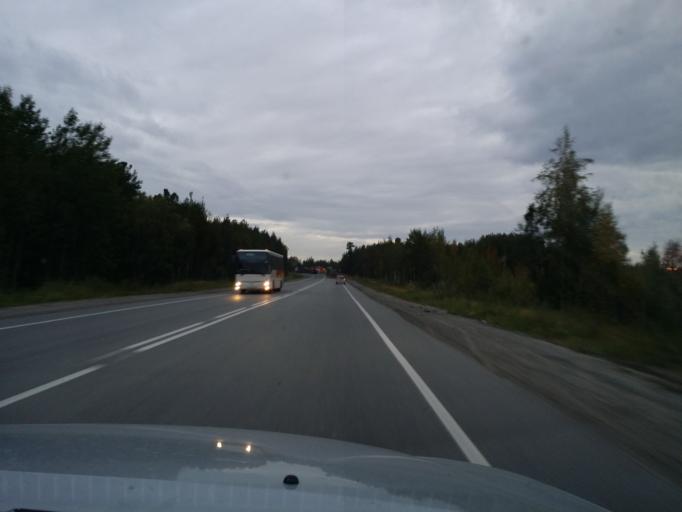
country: RU
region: Khanty-Mansiyskiy Avtonomnyy Okrug
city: Izluchinsk
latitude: 61.0140
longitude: 76.7865
